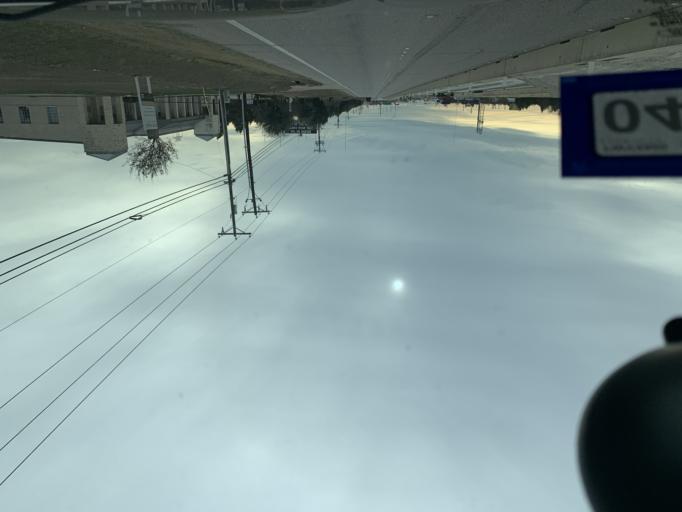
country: US
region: Texas
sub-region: Dallas County
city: Shamrock
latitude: 32.6168
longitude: -96.9182
